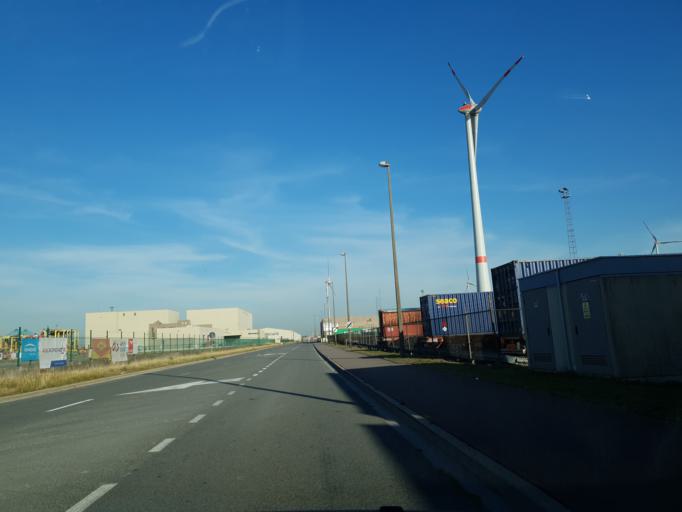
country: BE
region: Flanders
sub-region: Provincie Antwerpen
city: Stabroek
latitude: 51.3173
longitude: 4.3235
